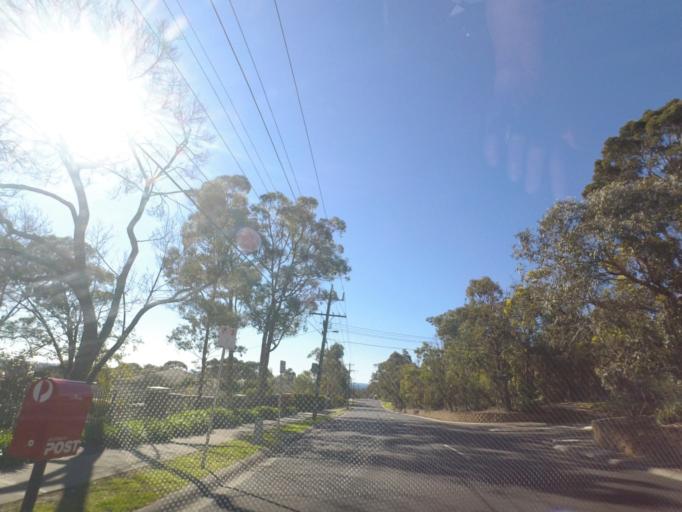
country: AU
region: Victoria
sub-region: Maroondah
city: Croydon Hills
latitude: -37.7824
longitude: 145.2741
